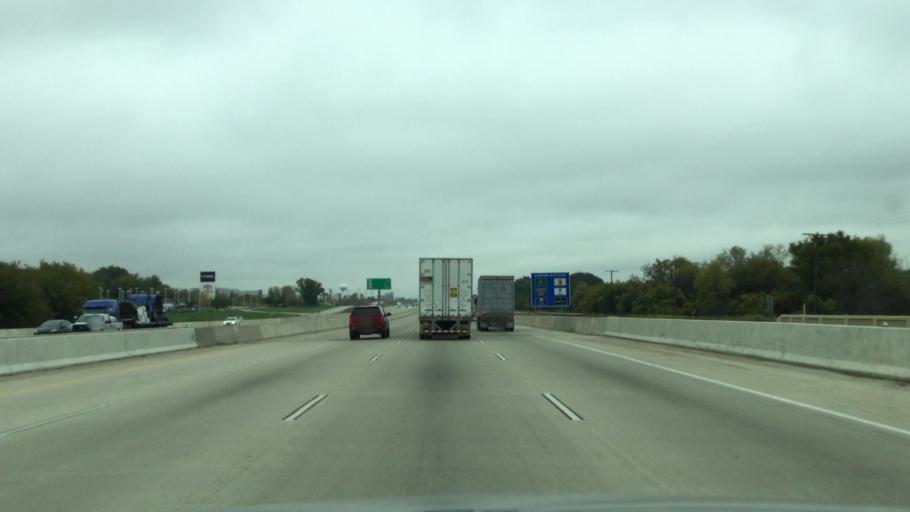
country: US
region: Wisconsin
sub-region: Kenosha County
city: Pleasant Prairie
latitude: 42.5540
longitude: -87.9523
